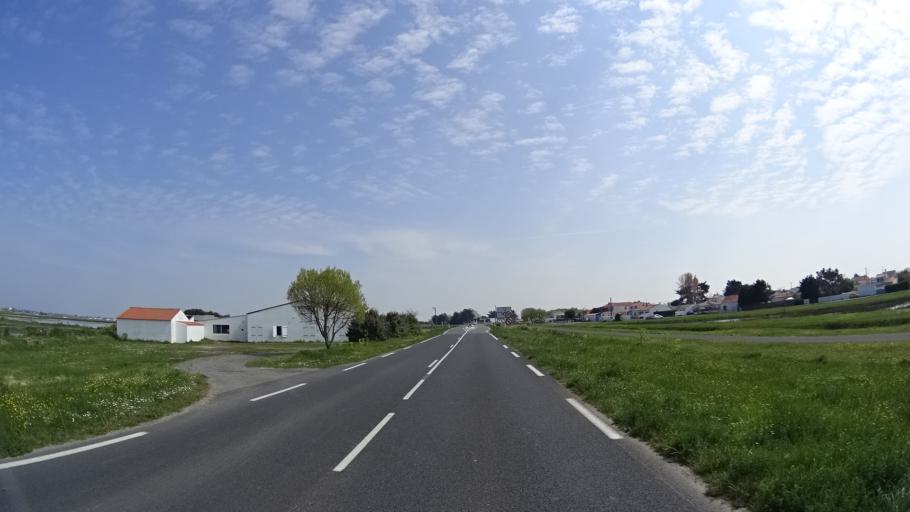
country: FR
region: Pays de la Loire
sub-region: Departement de la Vendee
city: La Gueriniere
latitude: 46.9833
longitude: -2.2680
